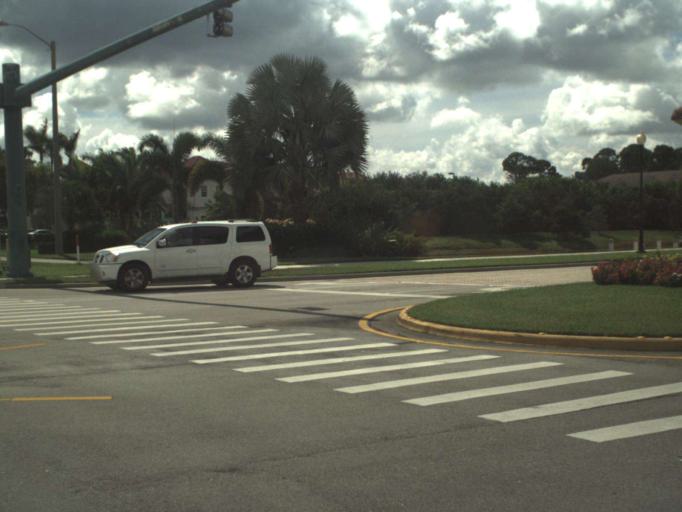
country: US
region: Florida
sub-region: Saint Lucie County
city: Port Saint Lucie
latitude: 27.3116
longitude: -80.4035
